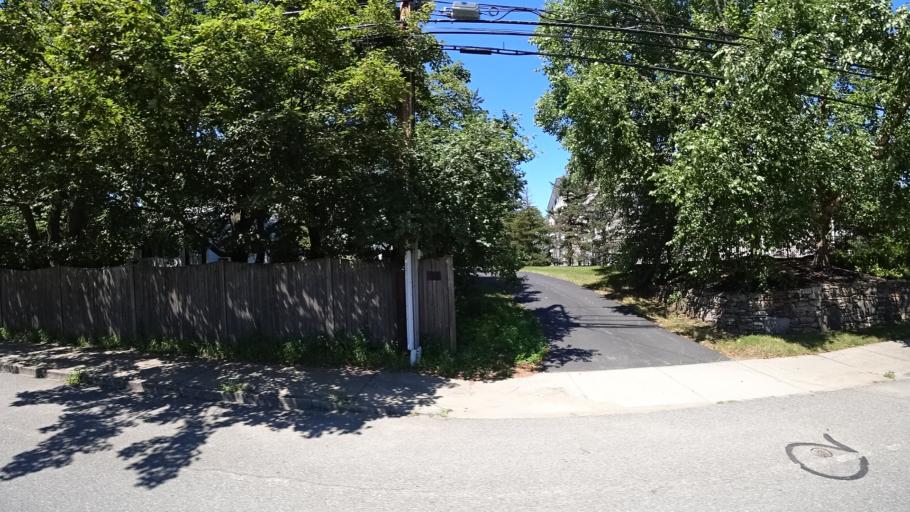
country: US
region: Massachusetts
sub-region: Norfolk County
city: Dedham
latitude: 42.2289
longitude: -71.1617
